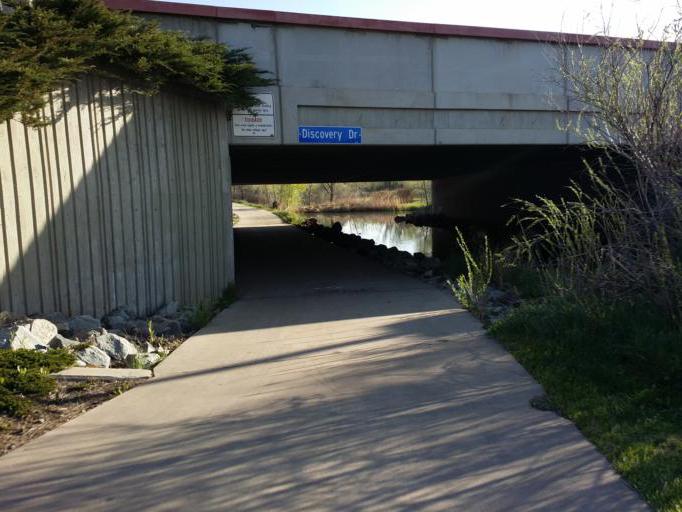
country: US
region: Colorado
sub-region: Boulder County
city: Boulder
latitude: 40.0096
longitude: -105.2455
